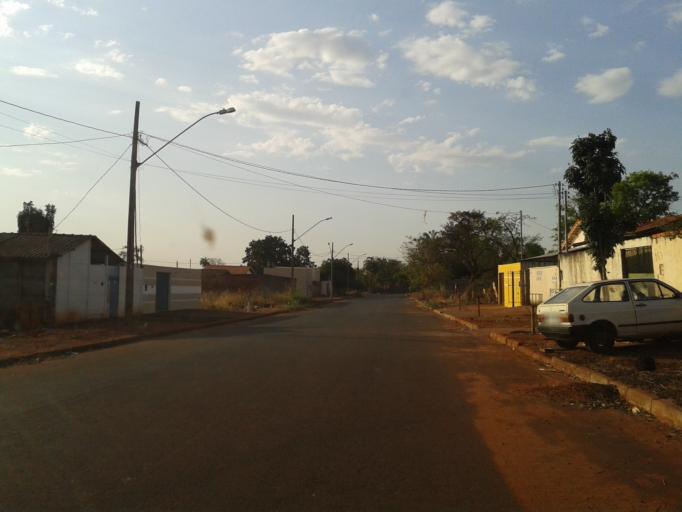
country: BR
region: Minas Gerais
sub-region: Ituiutaba
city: Ituiutaba
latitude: -18.9923
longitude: -49.4382
